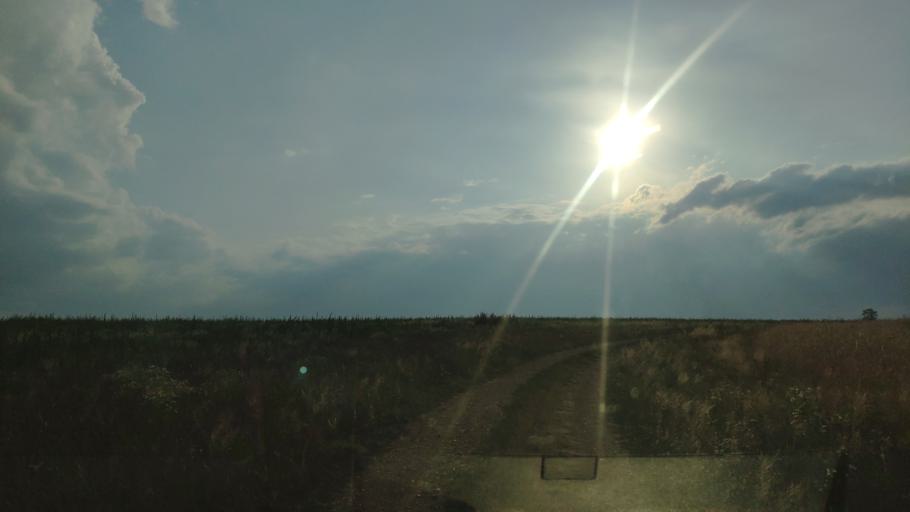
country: SK
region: Kosicky
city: Moldava nad Bodvou
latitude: 48.6933
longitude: 20.9991
